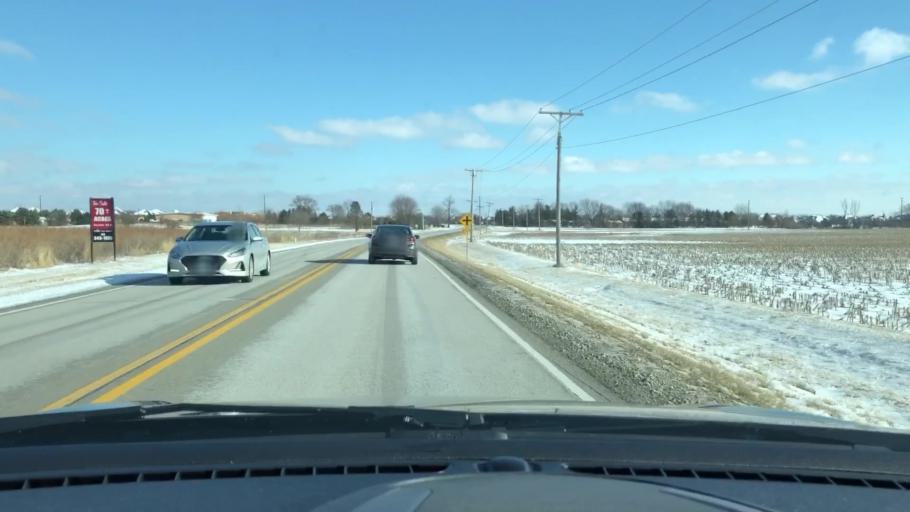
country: US
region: Illinois
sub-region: Will County
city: Mokena
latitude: 41.4840
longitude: -87.9102
